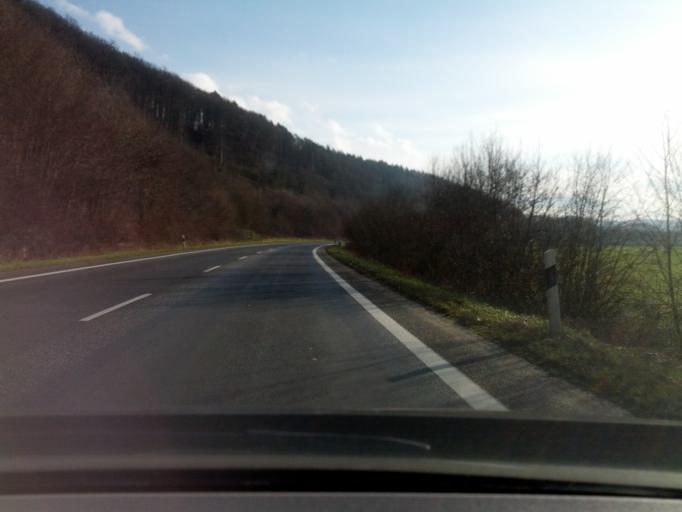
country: DE
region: Lower Saxony
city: Juhnde
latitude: 51.3893
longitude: 9.7942
